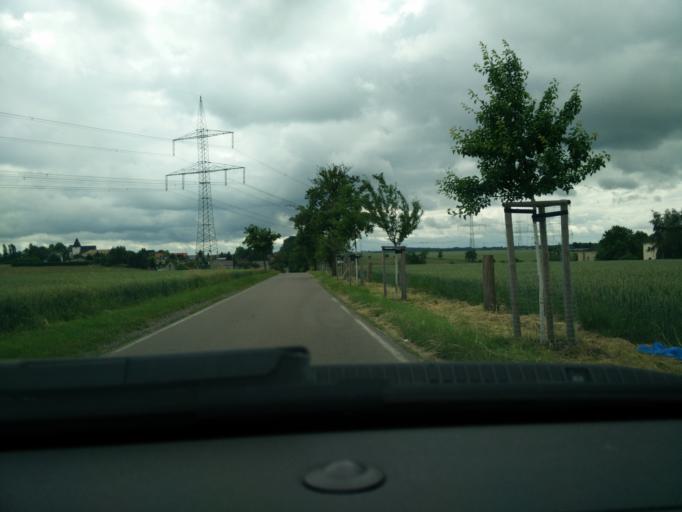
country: DE
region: Saxony
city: Geithain
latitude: 51.0883
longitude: 12.6523
